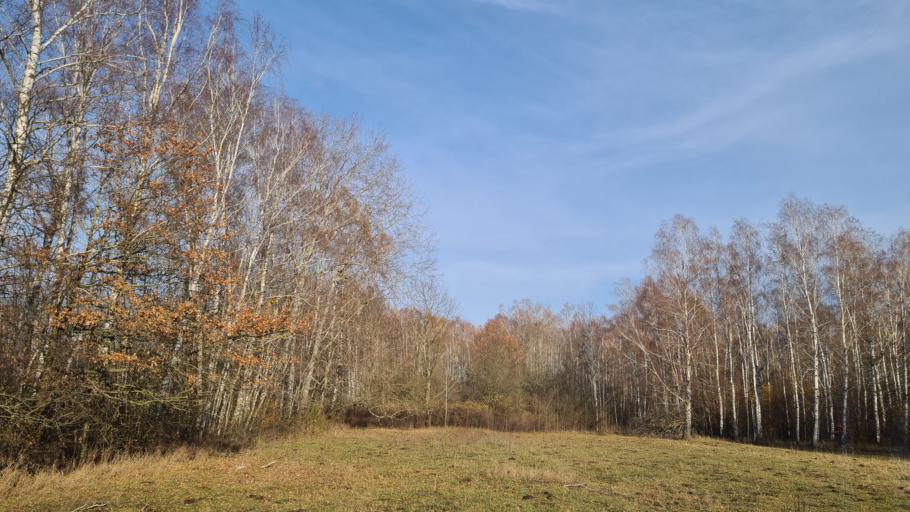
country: DE
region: Brandenburg
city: Sallgast
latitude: 51.5665
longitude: 13.8667
